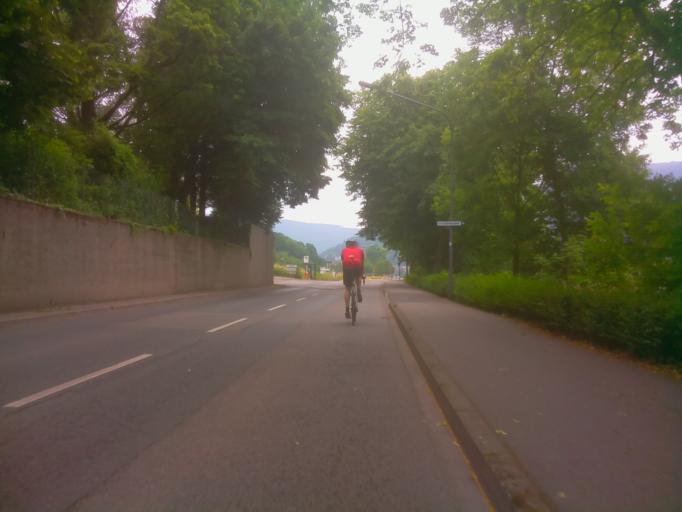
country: DE
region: Baden-Wuerttemberg
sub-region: Karlsruhe Region
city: Heidelberg
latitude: 49.4196
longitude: 8.7336
